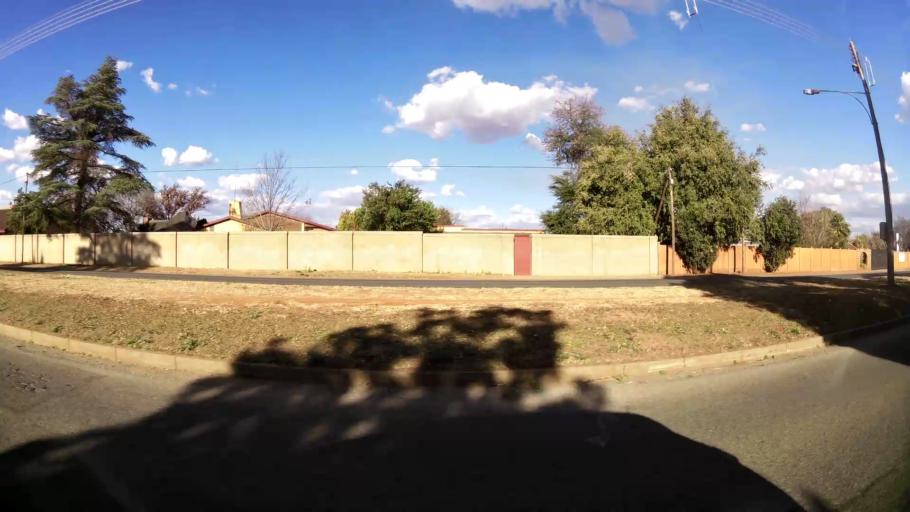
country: ZA
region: North-West
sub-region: Dr Kenneth Kaunda District Municipality
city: Klerksdorp
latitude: -26.8396
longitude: 26.6583
